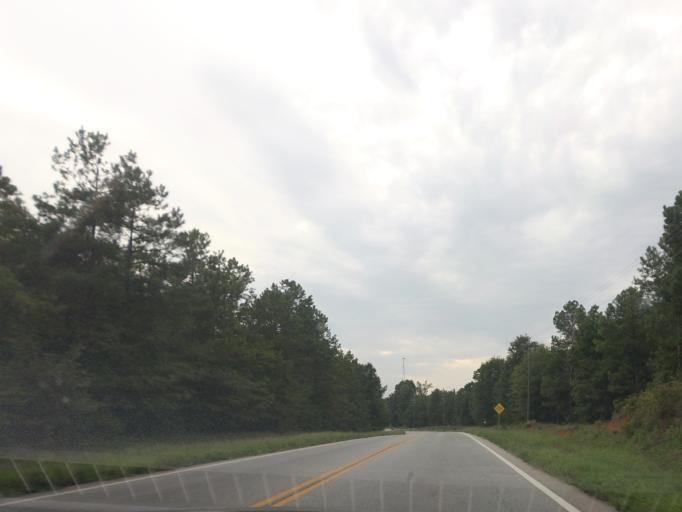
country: US
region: Georgia
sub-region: Twiggs County
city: Jeffersonville
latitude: 32.7651
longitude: -83.4706
